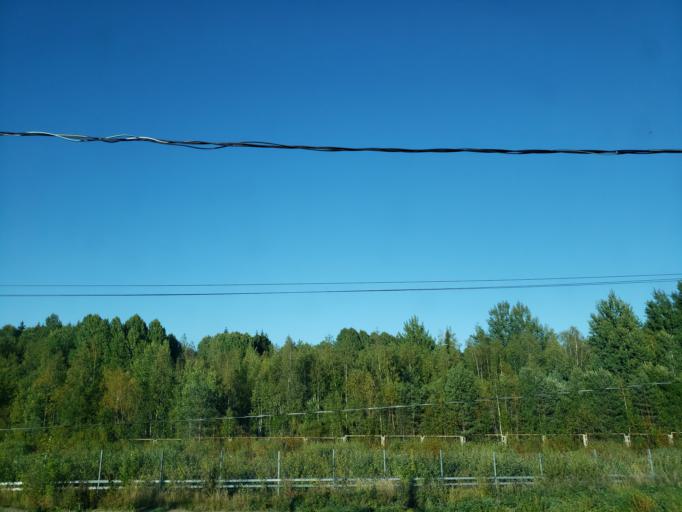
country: FI
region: South Karelia
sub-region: Lappeenranta
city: Nuijamaa
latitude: 60.8474
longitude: 28.3692
